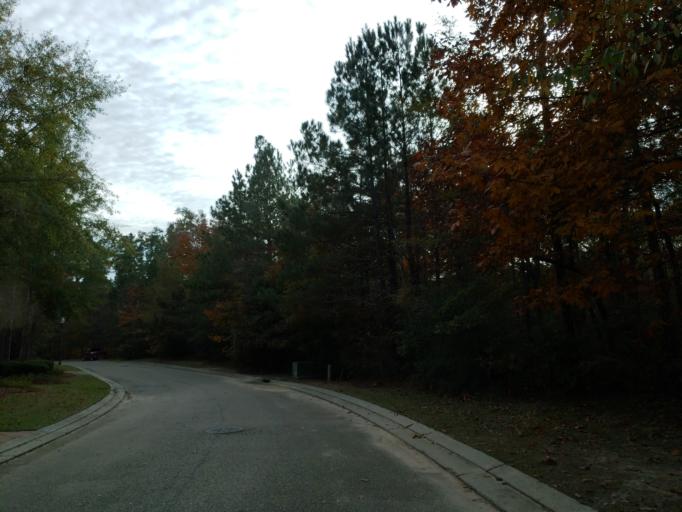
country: US
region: Mississippi
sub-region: Lamar County
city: West Hattiesburg
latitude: 31.2979
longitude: -89.3464
